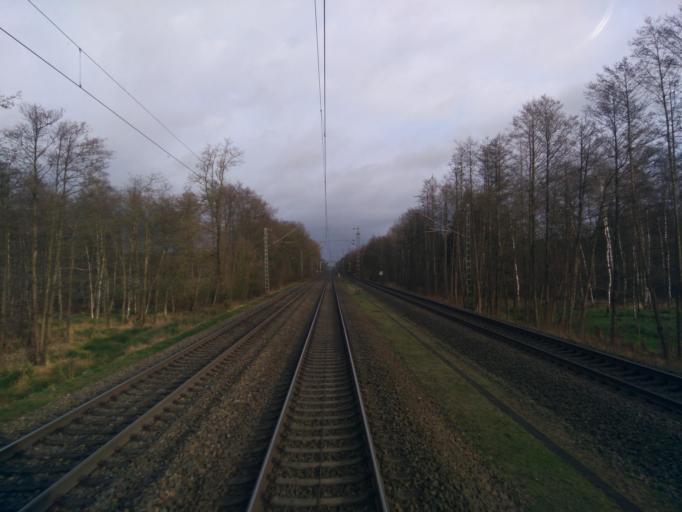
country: DE
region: Lower Saxony
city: Wistedt
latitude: 53.2586
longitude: 9.7029
